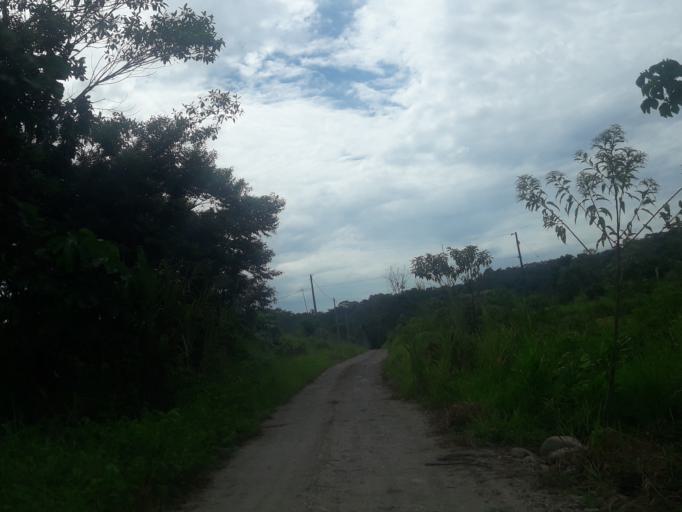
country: EC
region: Napo
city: Tena
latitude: -1.0574
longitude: -77.7971
